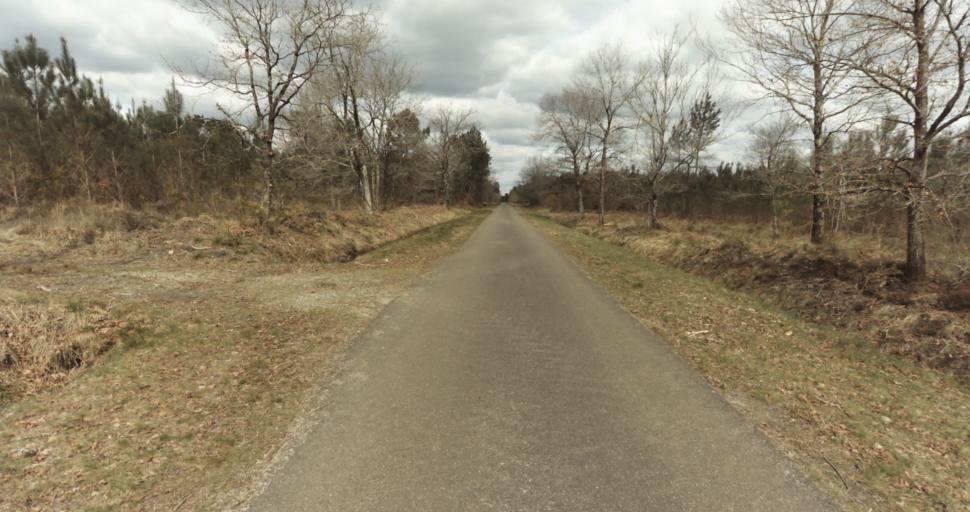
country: FR
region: Aquitaine
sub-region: Departement des Landes
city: Roquefort
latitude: 44.0966
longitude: -0.4541
